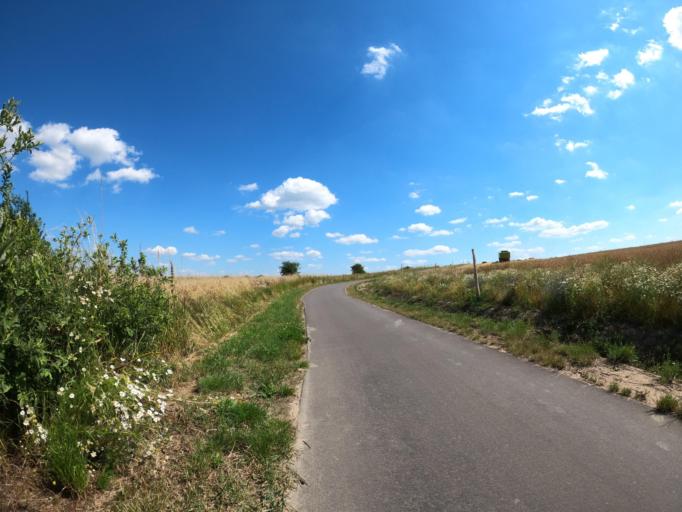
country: DE
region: Brandenburg
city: Mescherin
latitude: 53.2794
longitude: 14.4198
